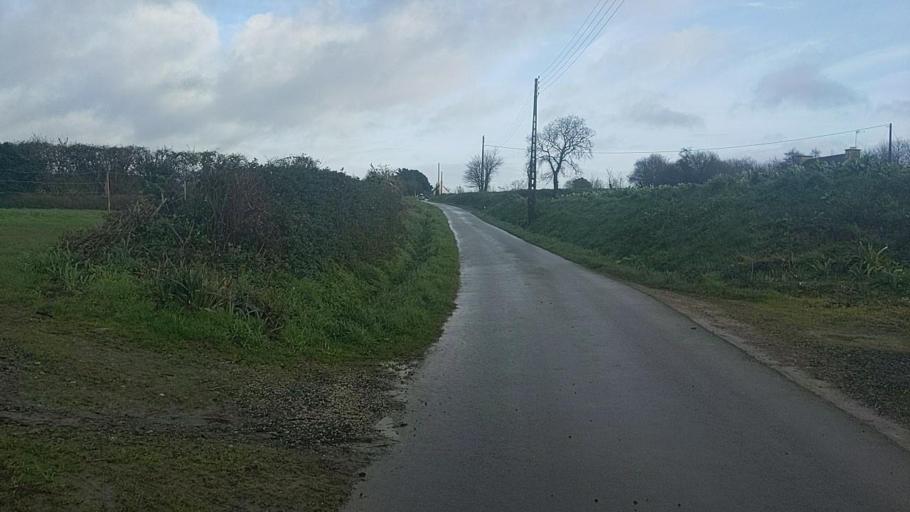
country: FR
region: Brittany
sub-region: Departement des Cotes-d'Armor
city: Pleubian
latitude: 48.8399
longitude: -3.1673
